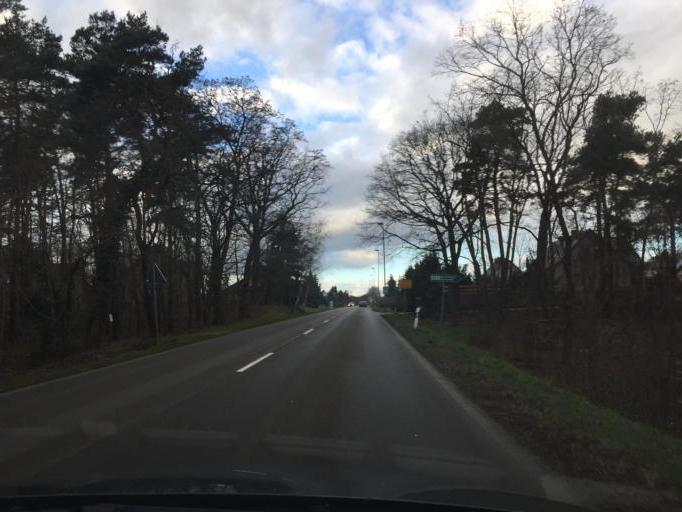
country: DE
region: Brandenburg
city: Kolkwitz
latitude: 51.7526
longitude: 14.1944
